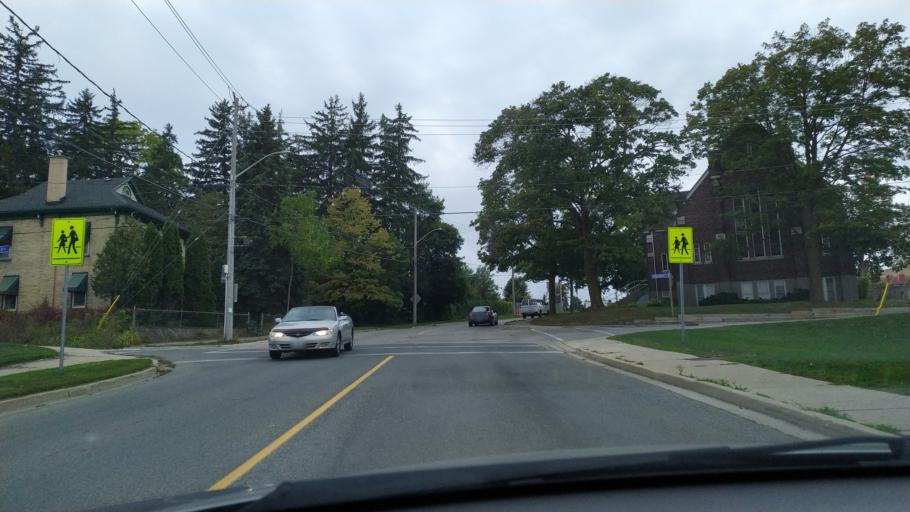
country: CA
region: Ontario
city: Waterloo
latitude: 43.4827
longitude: -80.4842
